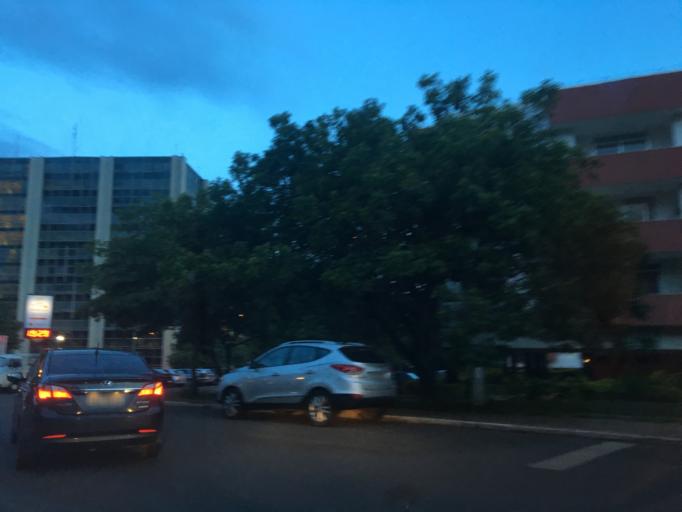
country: BR
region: Federal District
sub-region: Brasilia
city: Brasilia
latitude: -15.8056
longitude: -47.8844
